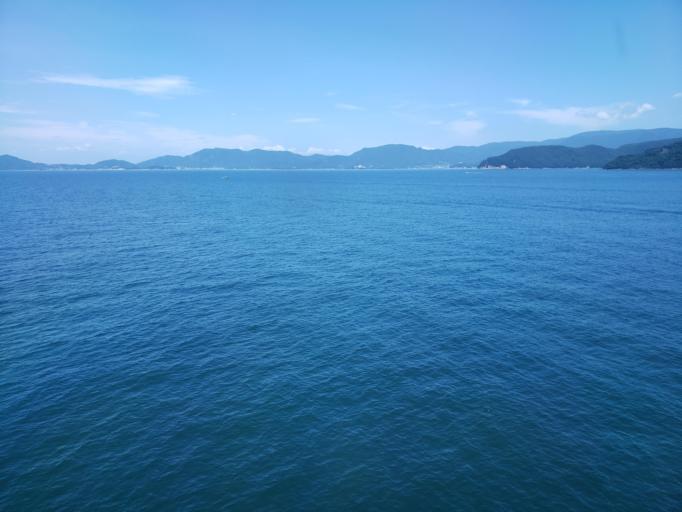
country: JP
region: Kagawa
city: Tonosho
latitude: 34.4081
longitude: 134.2147
